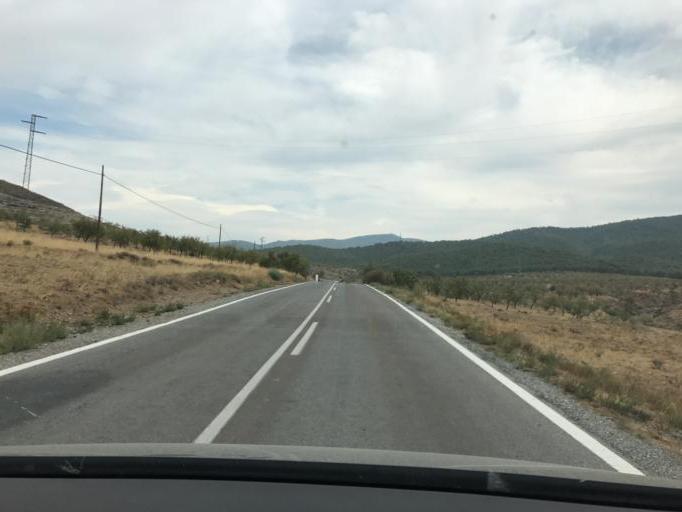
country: ES
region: Andalusia
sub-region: Provincia de Granada
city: Ferreira
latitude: 37.1792
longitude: -3.0578
